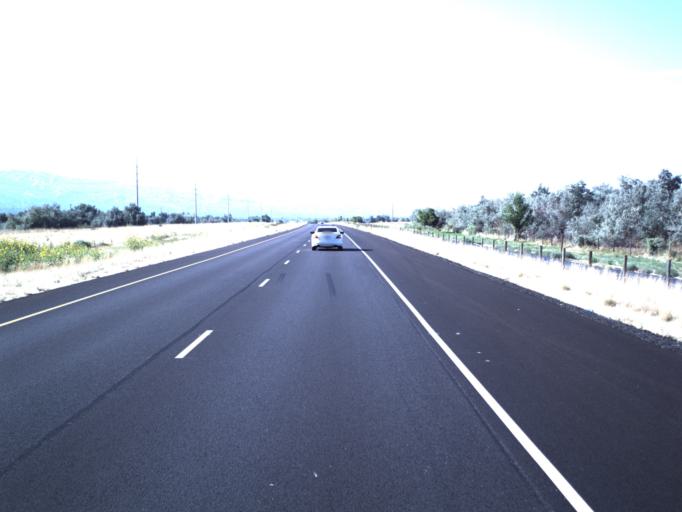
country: US
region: Utah
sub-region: Davis County
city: Farmington
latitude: 40.9552
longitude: -111.8932
